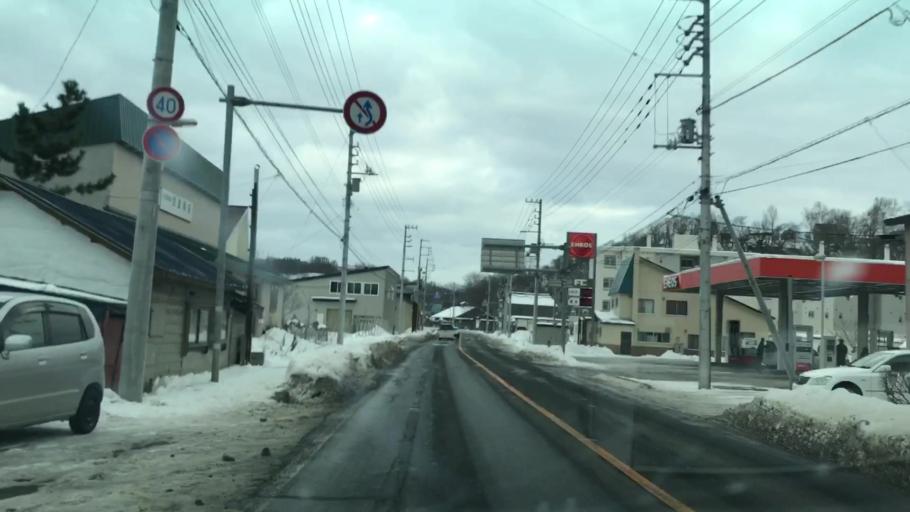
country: JP
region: Hokkaido
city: Yoichi
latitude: 43.2014
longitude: 140.7766
